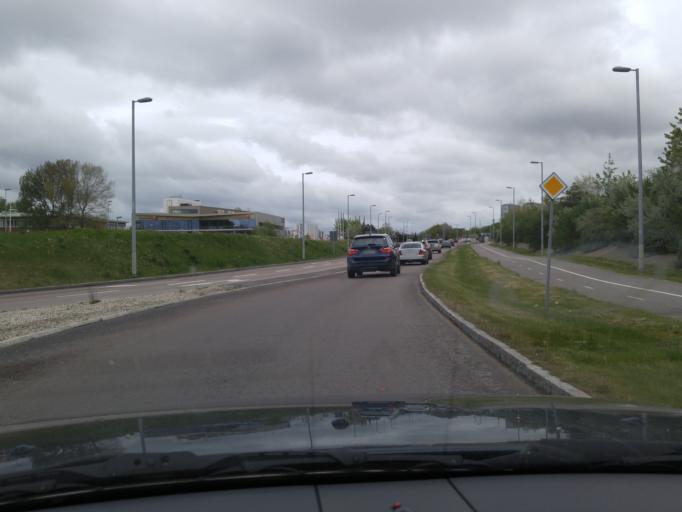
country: SE
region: Vaestra Goetaland
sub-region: Goteborg
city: Majorna
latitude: 57.6441
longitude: 11.9174
